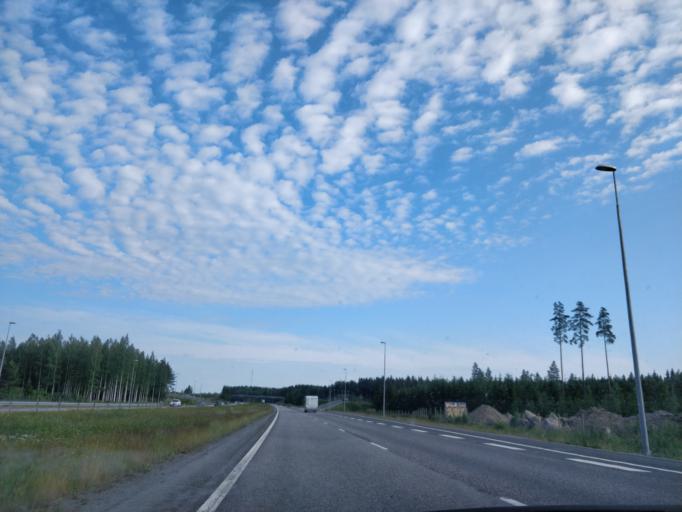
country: FI
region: Haeme
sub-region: Riihimaeki
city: Riihimaeki
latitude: 60.6933
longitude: 24.7448
